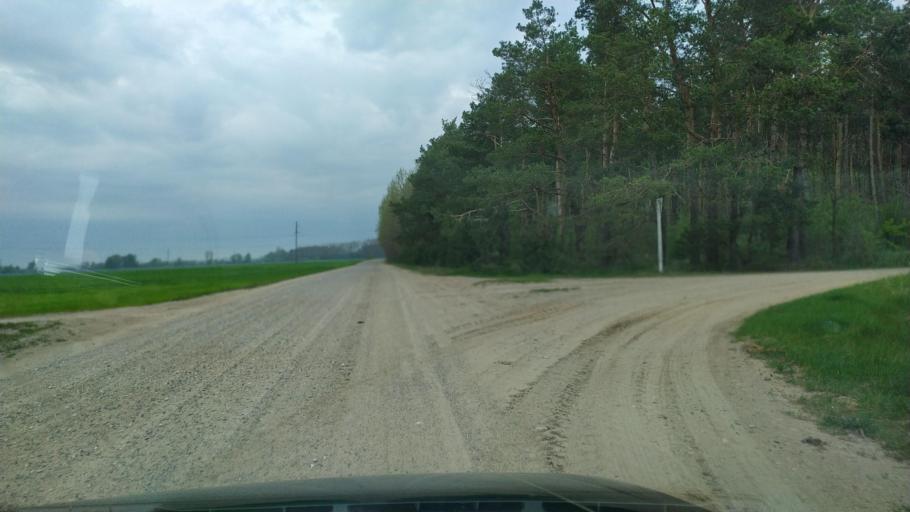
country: BY
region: Brest
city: Zhabinka
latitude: 52.1459
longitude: 24.0941
